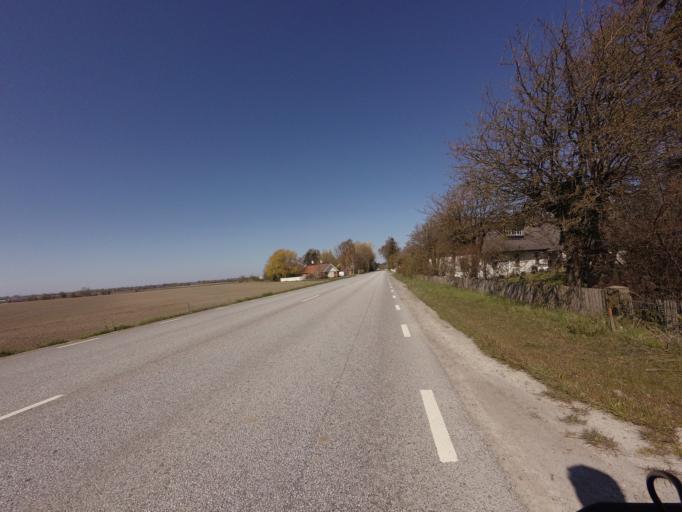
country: SE
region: Skane
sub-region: Vellinge Kommun
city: Vellinge
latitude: 55.4678
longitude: 13.0541
